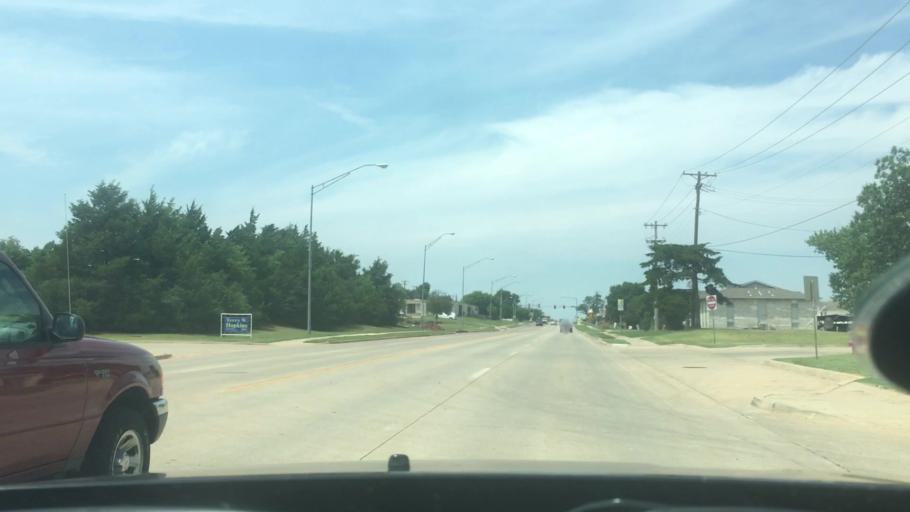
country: US
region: Oklahoma
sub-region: Pottawatomie County
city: Shawnee
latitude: 35.3617
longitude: -96.9174
